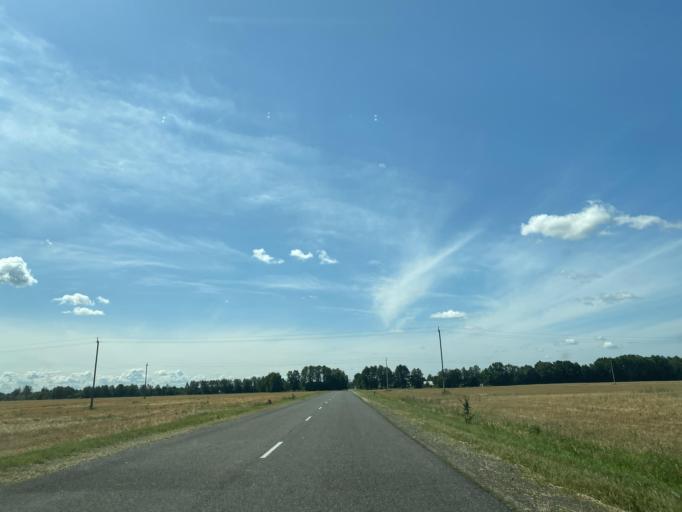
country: BY
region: Brest
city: Ivanava
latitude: 52.1949
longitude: 25.6122
